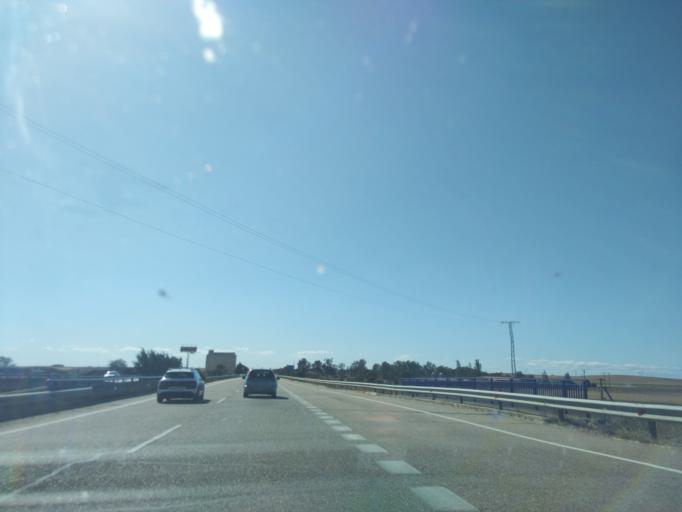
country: ES
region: Castille and Leon
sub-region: Provincia de Zamora
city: Cerecinos de Campos
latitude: 41.9036
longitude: -5.4821
